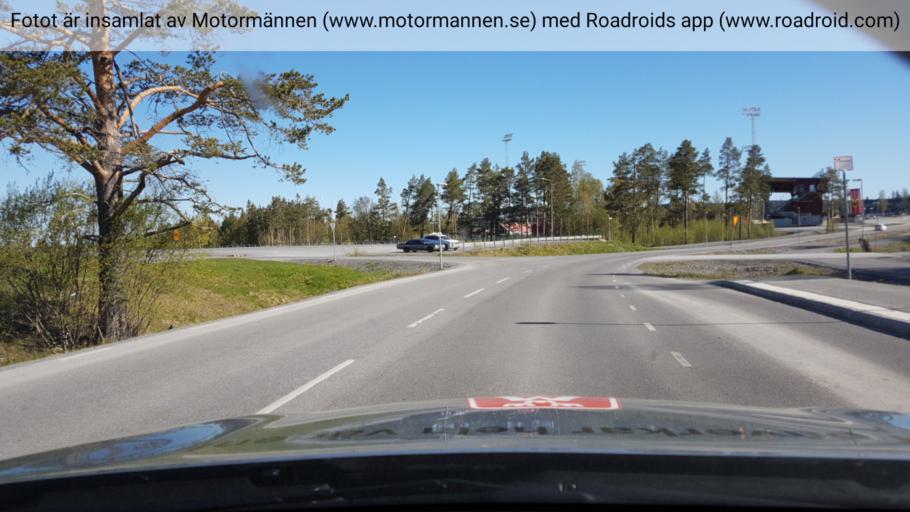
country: SE
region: Jaemtland
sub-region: OEstersunds Kommun
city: Ostersund
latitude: 63.1921
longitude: 14.6529
